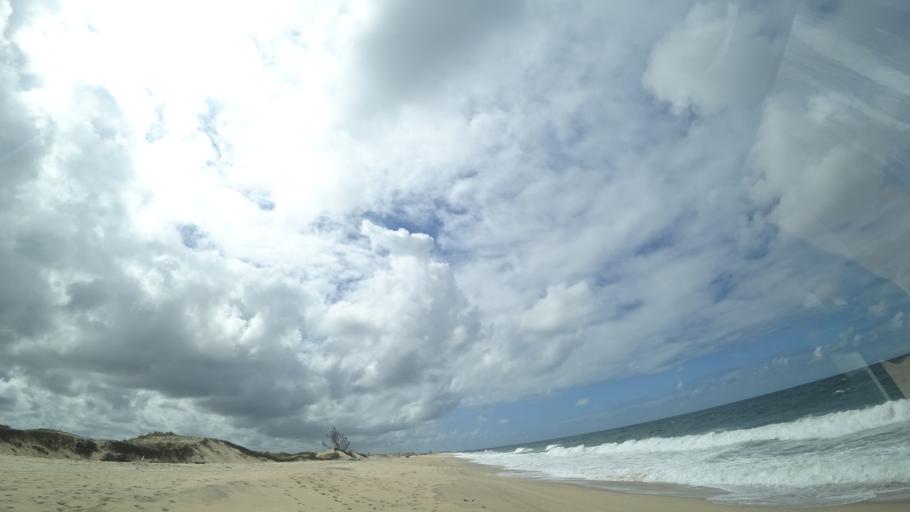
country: MZ
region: Sofala
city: Beira
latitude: -19.6182
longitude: 35.2173
